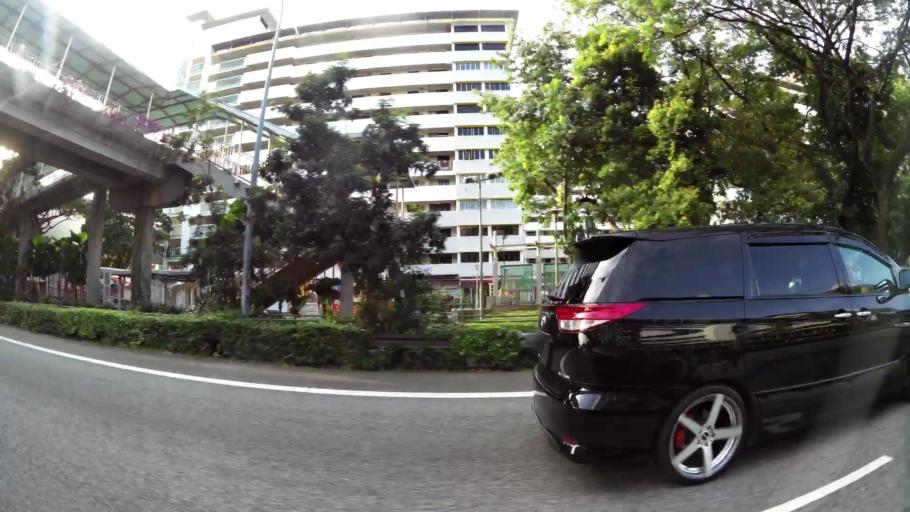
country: SG
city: Singapore
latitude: 1.3220
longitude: 103.8861
